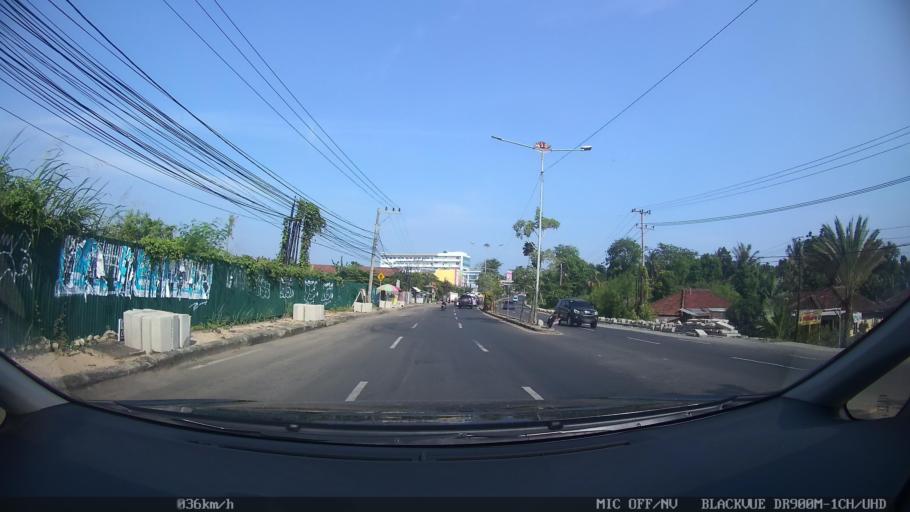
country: ID
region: Lampung
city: Kedaton
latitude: -5.3675
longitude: 105.2326
